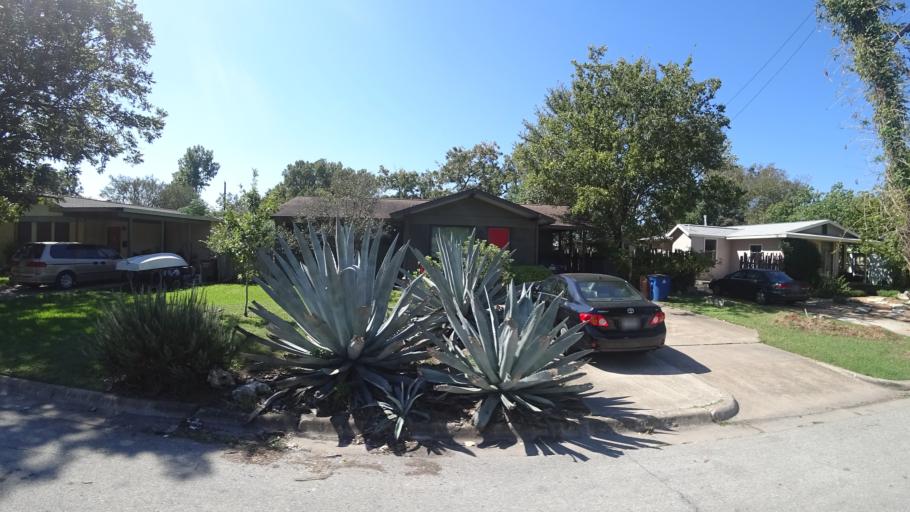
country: US
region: Texas
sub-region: Travis County
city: Austin
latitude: 30.3089
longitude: -97.7028
